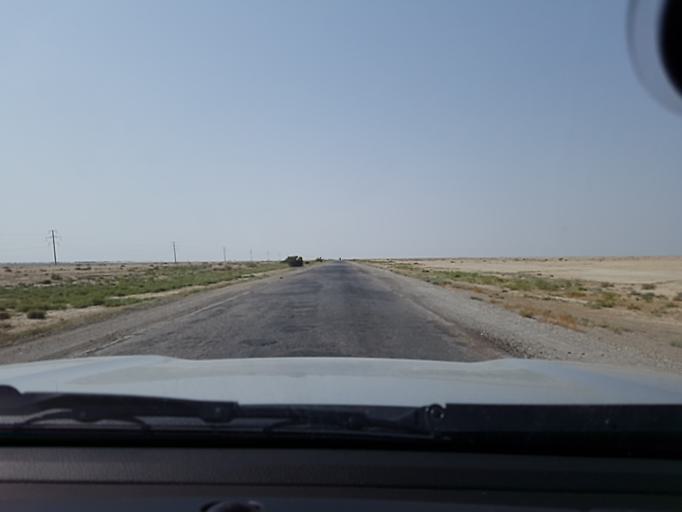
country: TM
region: Balkan
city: Gumdag
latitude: 38.8830
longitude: 54.5934
